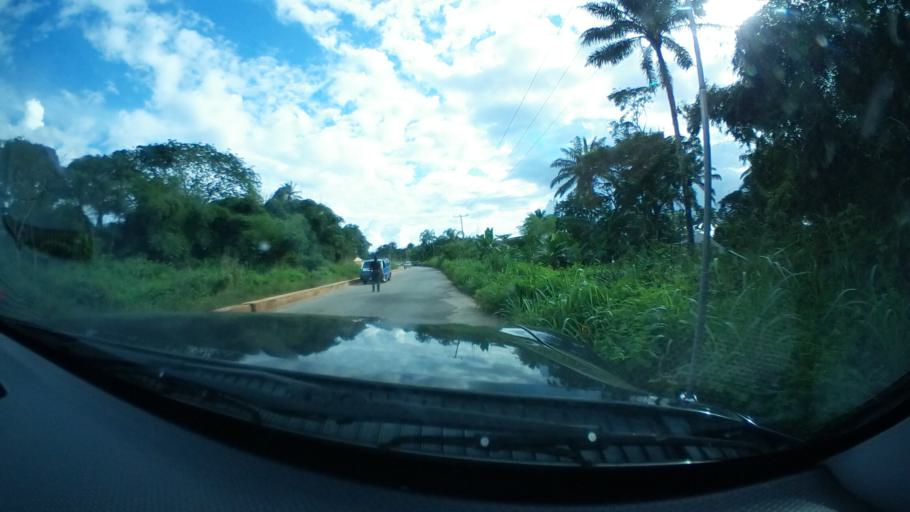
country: NG
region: Anambra
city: Uga
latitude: 5.8713
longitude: 7.1015
